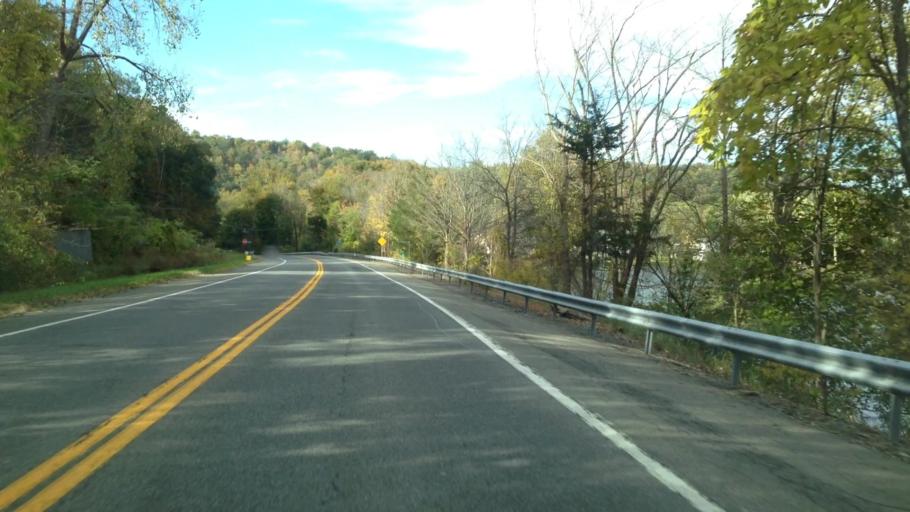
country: US
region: New York
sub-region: Ulster County
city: Kingston
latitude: 41.8916
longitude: -74.0164
